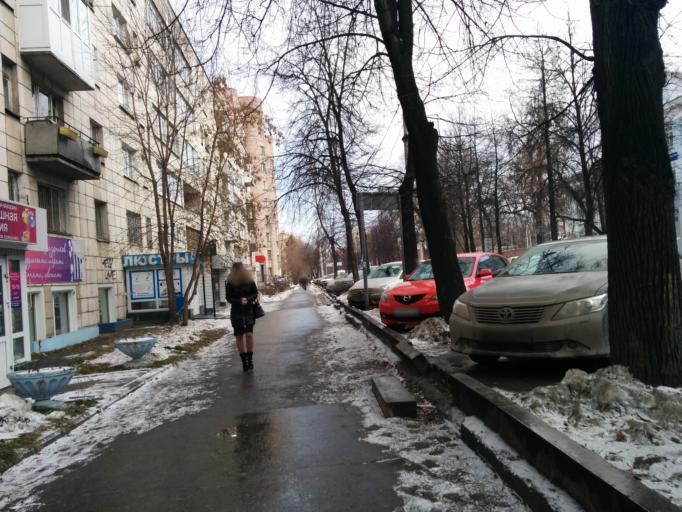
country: RU
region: Perm
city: Perm
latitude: 58.0124
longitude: 56.2518
